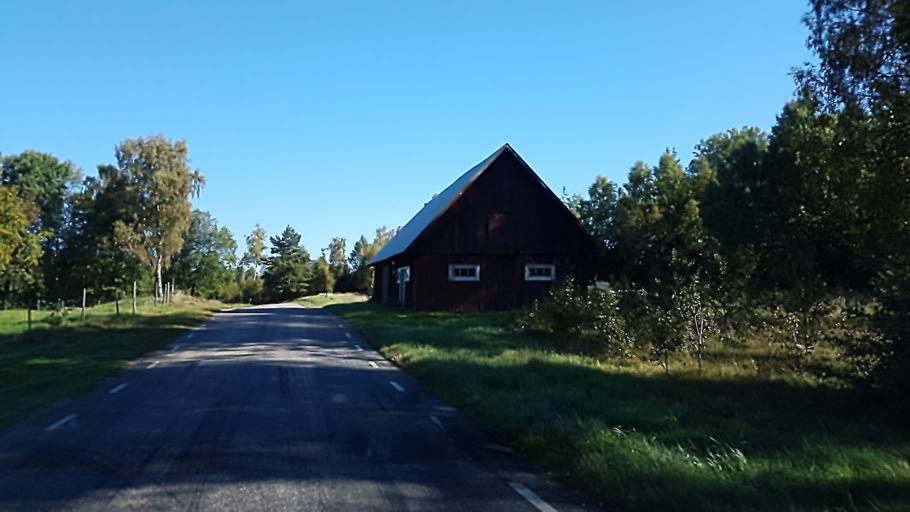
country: SE
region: Kronoberg
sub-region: Ljungby Kommun
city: Ljungby
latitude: 56.8198
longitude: 14.0465
